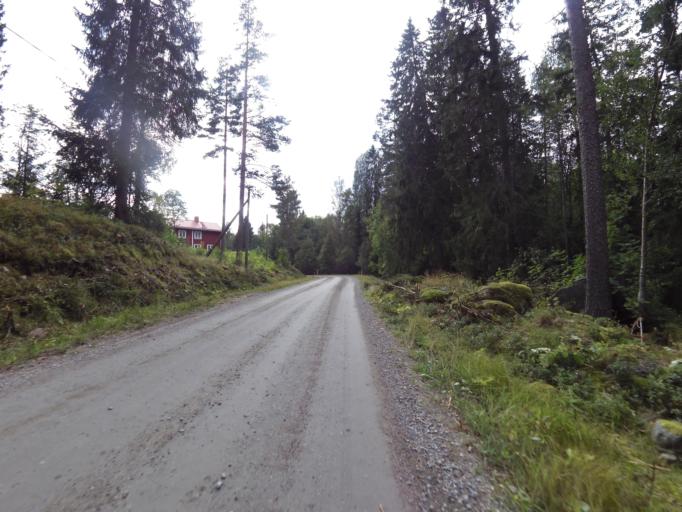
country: SE
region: Gaevleborg
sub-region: Sandvikens Kommun
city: Sandviken
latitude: 60.7304
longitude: 16.8201
